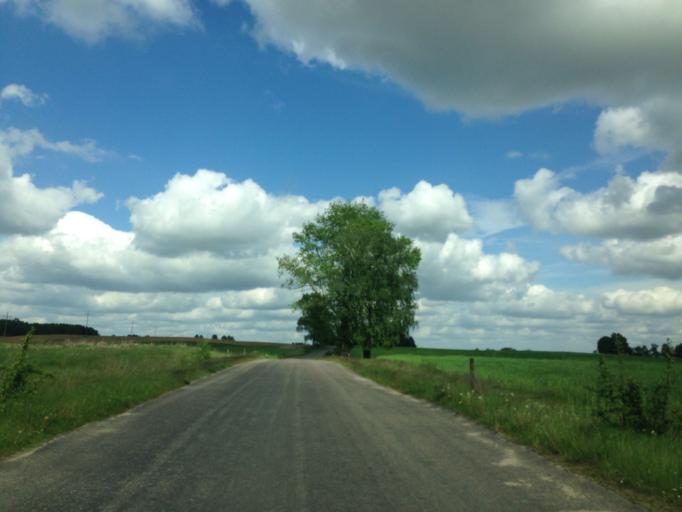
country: PL
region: Warmian-Masurian Voivodeship
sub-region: Powiat nidzicki
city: Kozlowo
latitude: 53.3955
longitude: 20.2165
